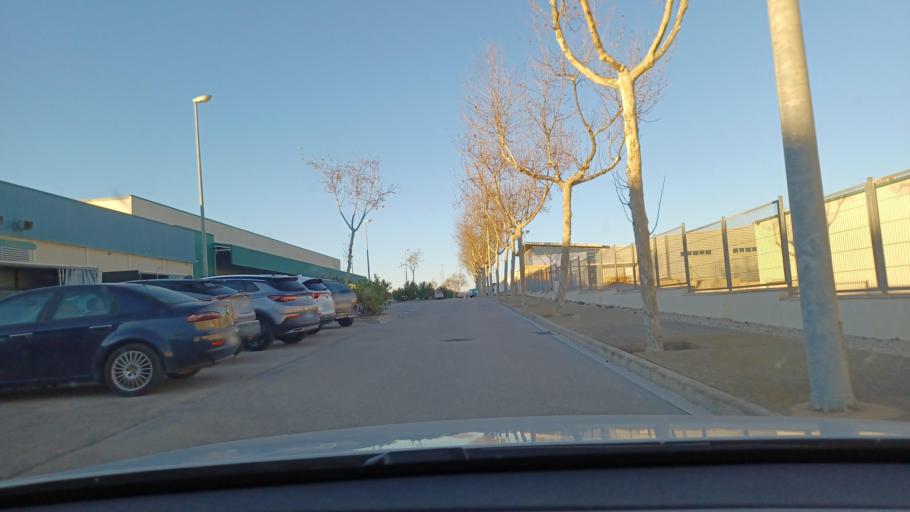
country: ES
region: Catalonia
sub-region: Provincia de Tarragona
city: Amposta
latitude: 40.7029
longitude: 0.5601
